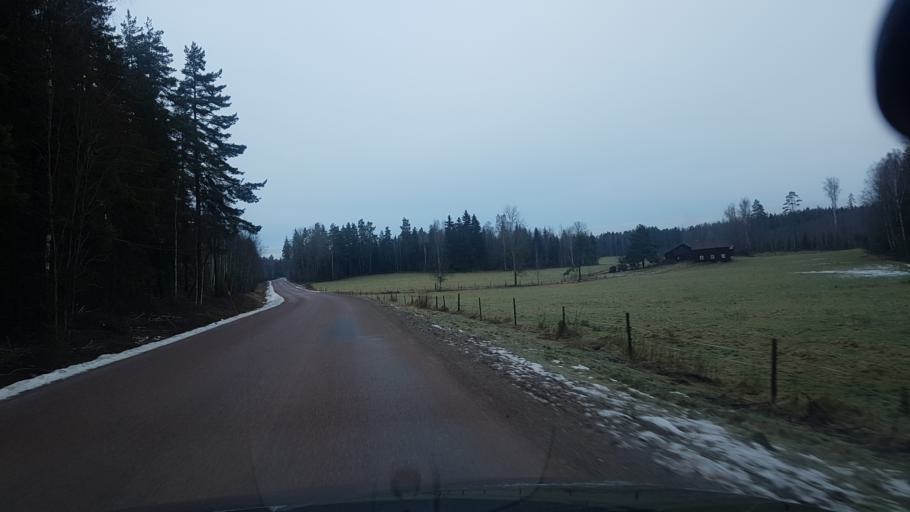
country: SE
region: Dalarna
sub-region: Borlange Kommun
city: Ornas
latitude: 60.4566
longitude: 15.6169
